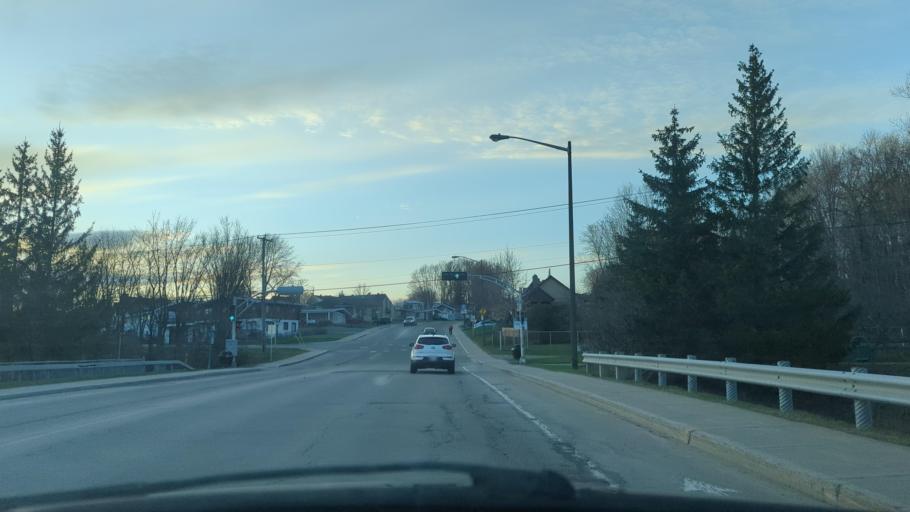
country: CA
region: Quebec
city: Quebec
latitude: 46.8493
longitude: -71.2611
